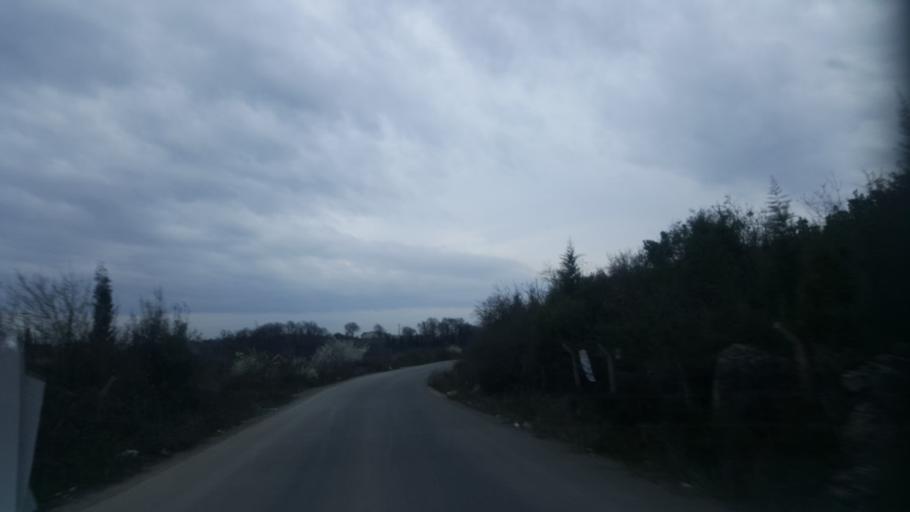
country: TR
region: Kocaeli
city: Tavsanli
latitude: 40.8411
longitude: 29.5534
